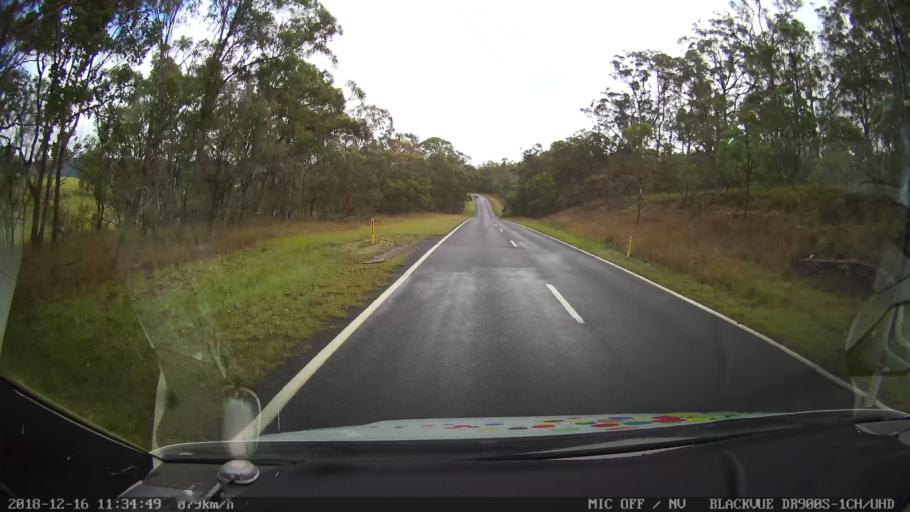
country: AU
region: New South Wales
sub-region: Tenterfield Municipality
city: Carrolls Creek
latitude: -28.9962
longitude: 152.1578
